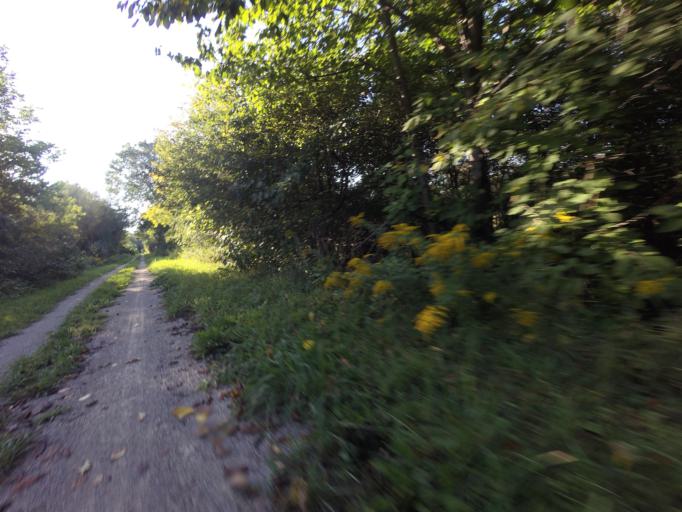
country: CA
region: Ontario
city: Goderich
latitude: 43.7483
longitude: -81.6479
